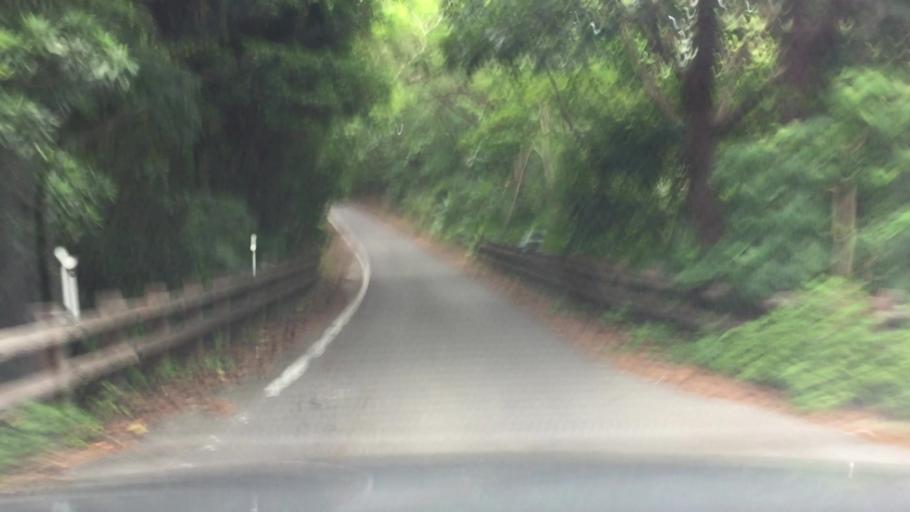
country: JP
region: Okinawa
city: Ishigaki
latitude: 24.4517
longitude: 124.1365
